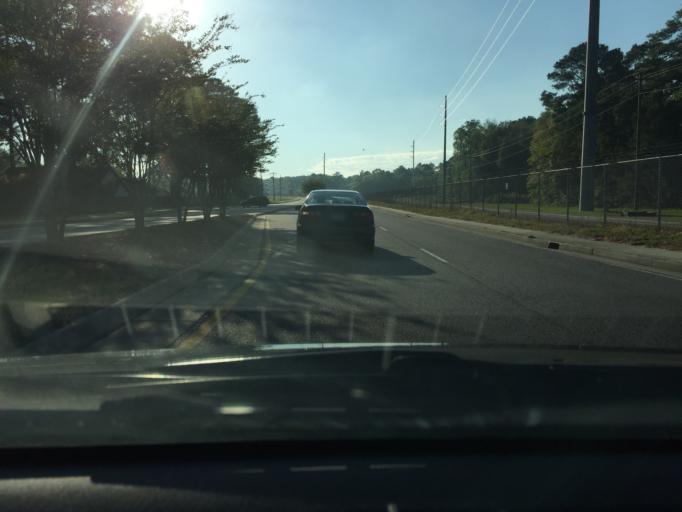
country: US
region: Georgia
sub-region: Chatham County
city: Montgomery
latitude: 32.0022
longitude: -81.1388
